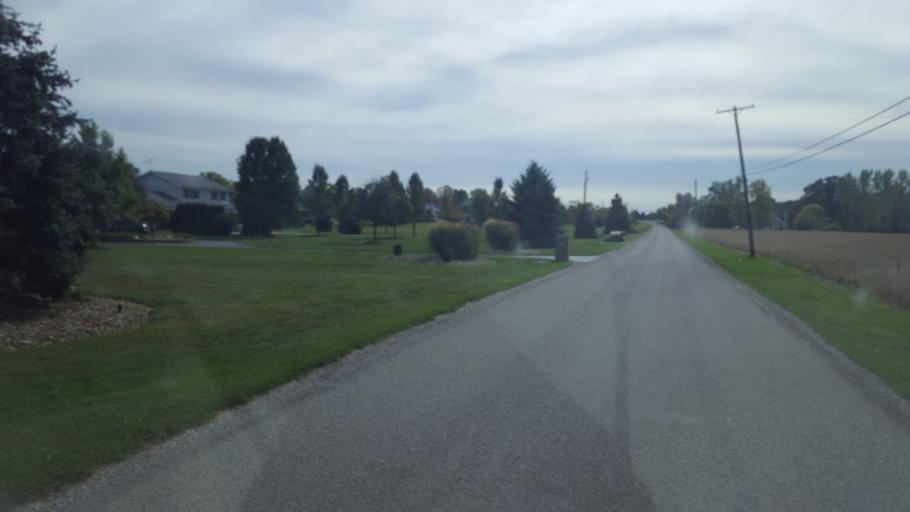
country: US
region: Ohio
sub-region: Lorain County
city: Vermilion-on-the-Lake
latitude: 41.3790
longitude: -82.3300
